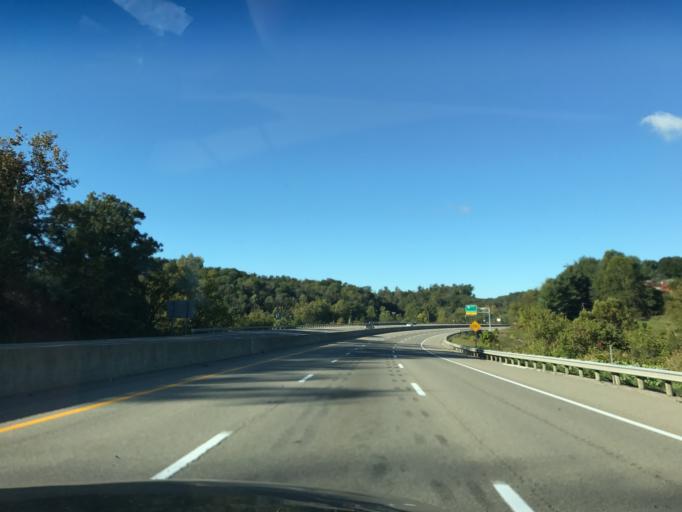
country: US
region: West Virginia
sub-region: Wood County
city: Blennerhassett
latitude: 39.2524
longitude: -81.6003
